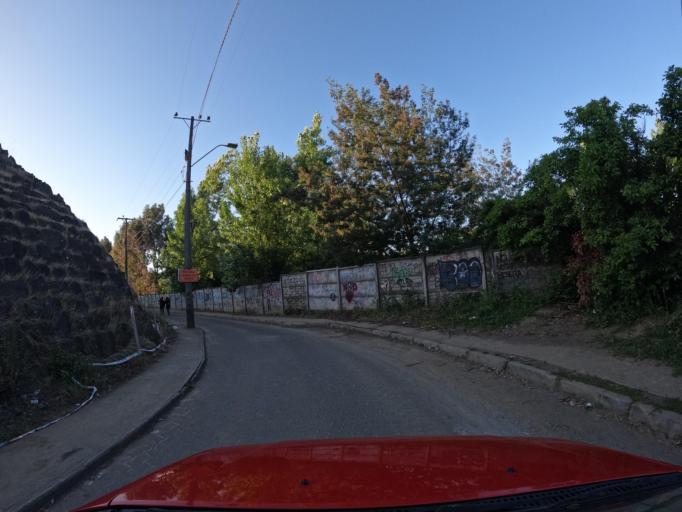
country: CL
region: Biobio
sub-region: Provincia de Concepcion
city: Lota
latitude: -37.1688
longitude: -72.9406
